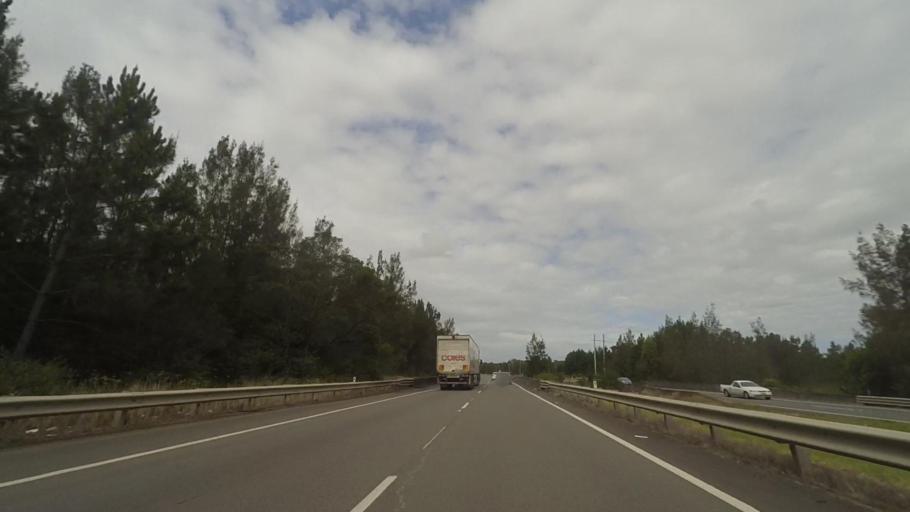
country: AU
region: New South Wales
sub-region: Port Stephens Shire
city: Raymond Terrace
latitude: -32.7788
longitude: 151.7494
